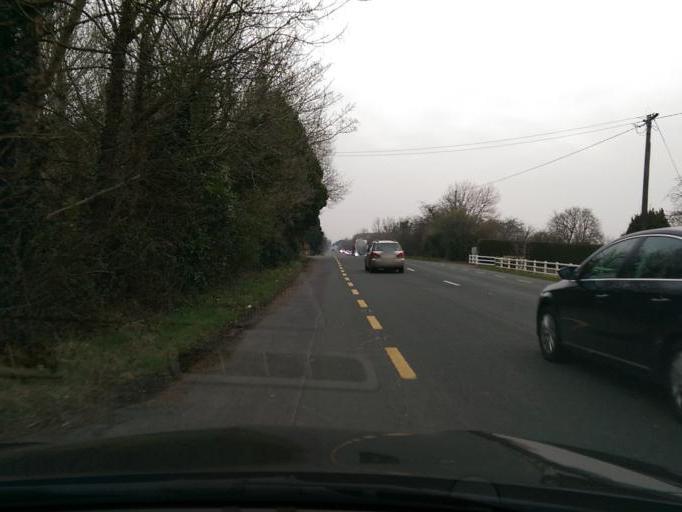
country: IE
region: Leinster
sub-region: An Iarmhi
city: Athlone
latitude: 53.4344
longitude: -7.9680
